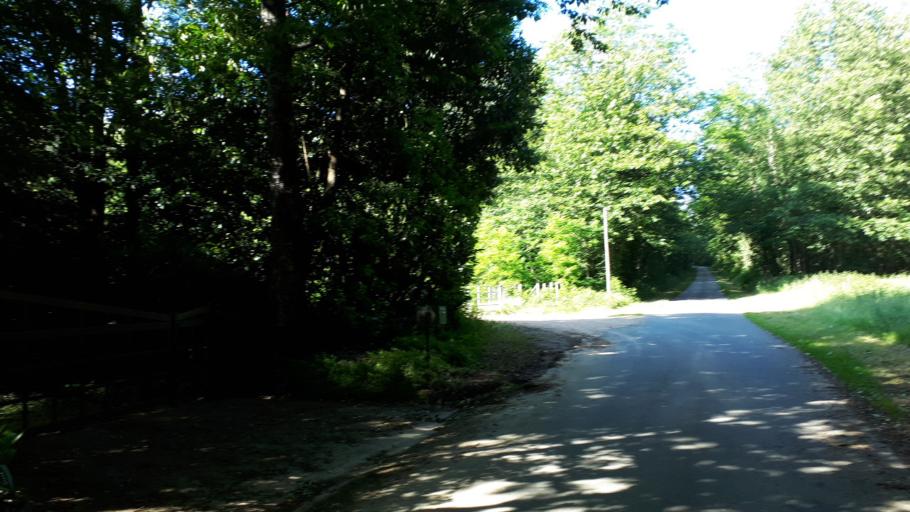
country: FR
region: Centre
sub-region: Departement du Loir-et-Cher
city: Sarge-sur-Braye
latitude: 47.9279
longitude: 0.8743
